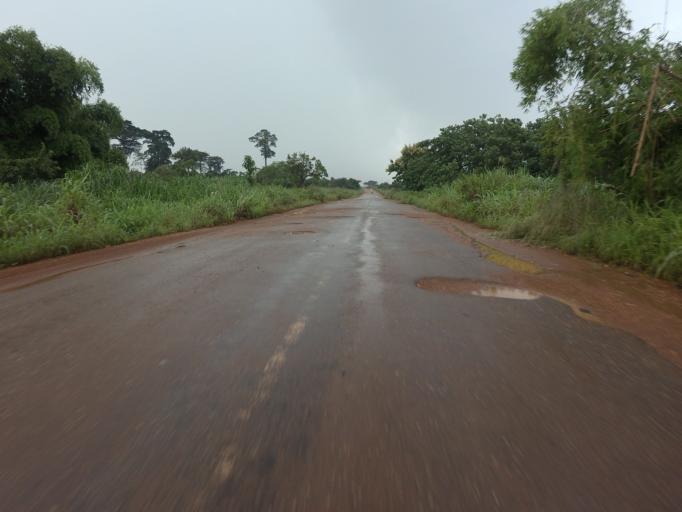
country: GH
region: Volta
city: Hohoe
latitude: 7.0592
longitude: 0.4297
